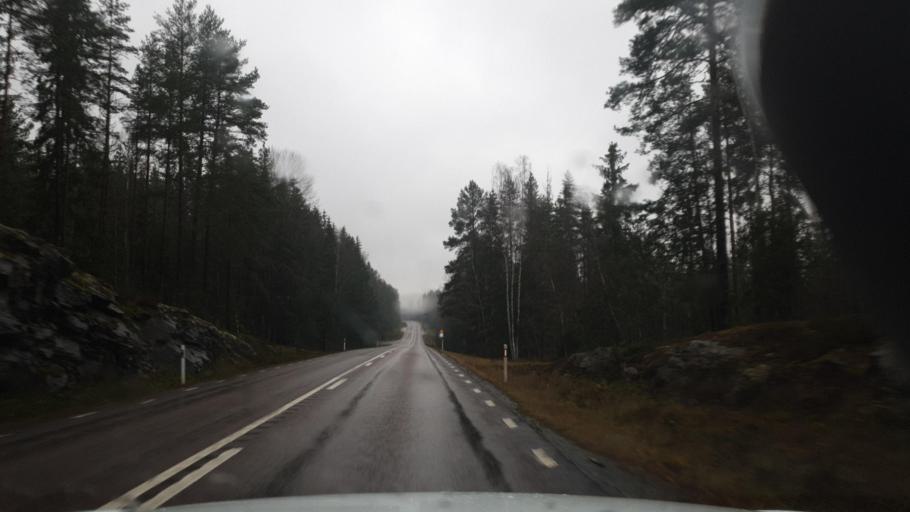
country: SE
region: Vaermland
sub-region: Karlstads Kommun
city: Edsvalla
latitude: 59.5890
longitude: 13.0115
